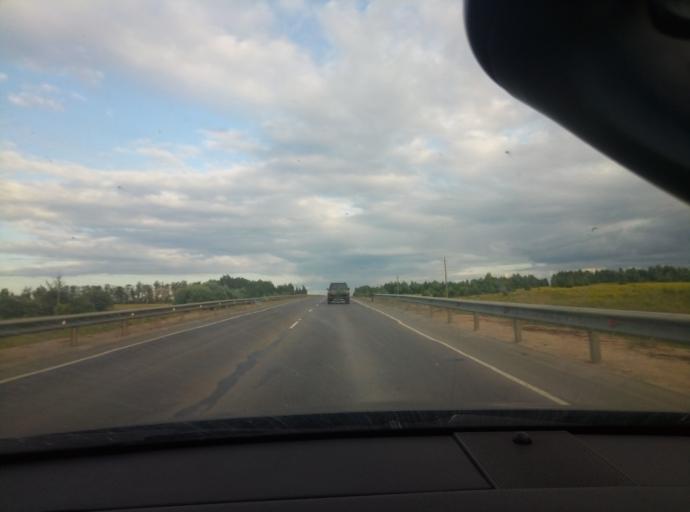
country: RU
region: Tula
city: Leninskiy
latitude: 54.2583
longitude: 37.3004
